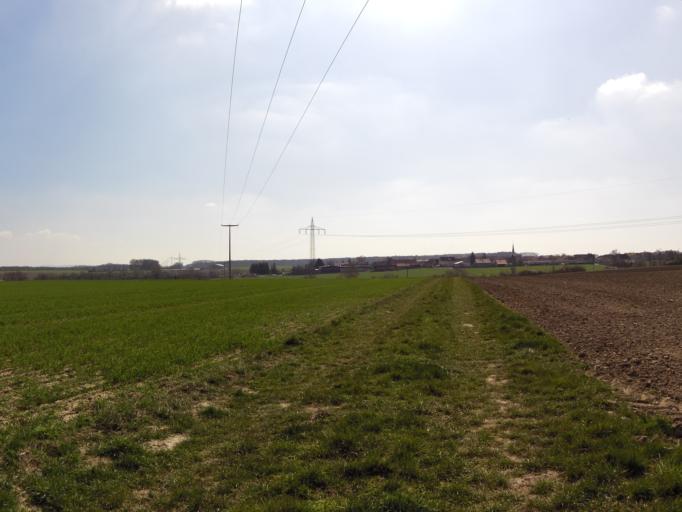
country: DE
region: Bavaria
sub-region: Regierungsbezirk Unterfranken
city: Biebelried
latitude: 49.7369
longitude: 10.0904
